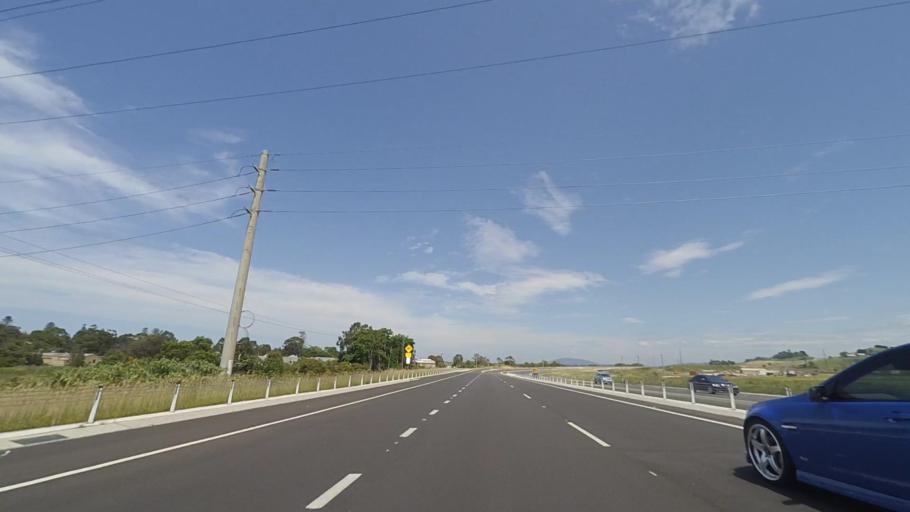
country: AU
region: New South Wales
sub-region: Kiama
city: Gerringong
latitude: -34.7412
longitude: 150.8197
